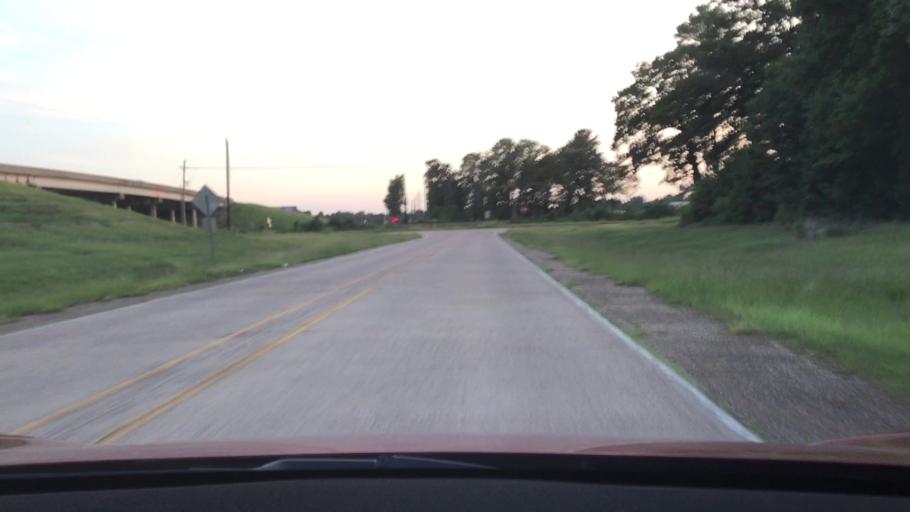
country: US
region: Louisiana
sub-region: Bossier Parish
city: Bossier City
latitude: 32.4023
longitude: -93.7350
